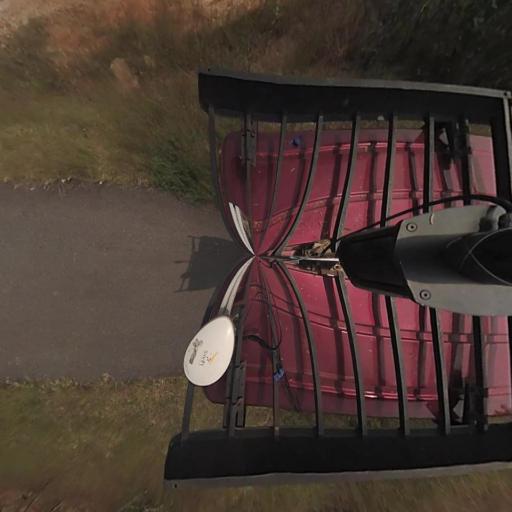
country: IN
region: Telangana
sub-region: Nalgonda
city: Nalgonda
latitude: 17.2006
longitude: 79.1430
